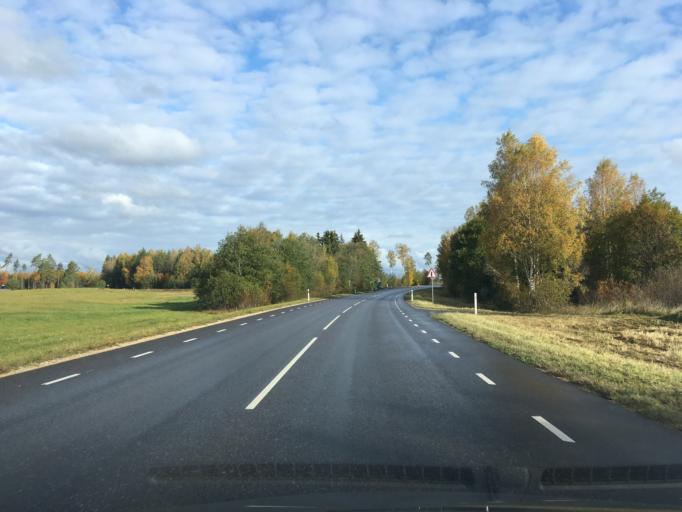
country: EE
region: Harju
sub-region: Raasiku vald
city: Raasiku
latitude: 59.2047
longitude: 25.1840
